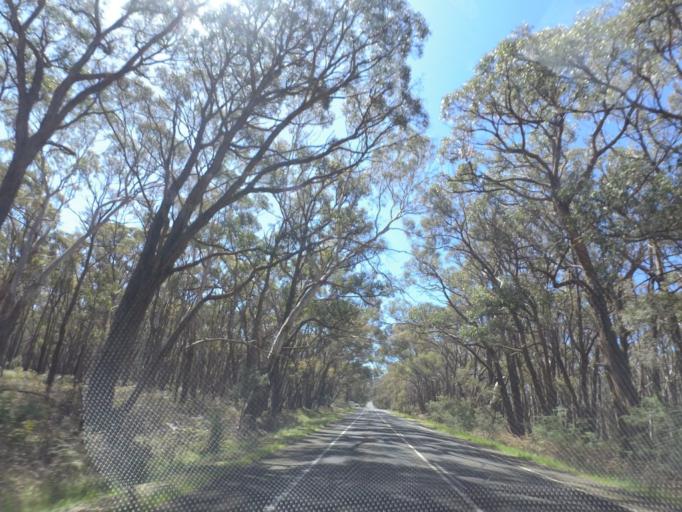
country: AU
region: Victoria
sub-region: Hume
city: Sunbury
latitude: -37.2362
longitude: 144.7389
